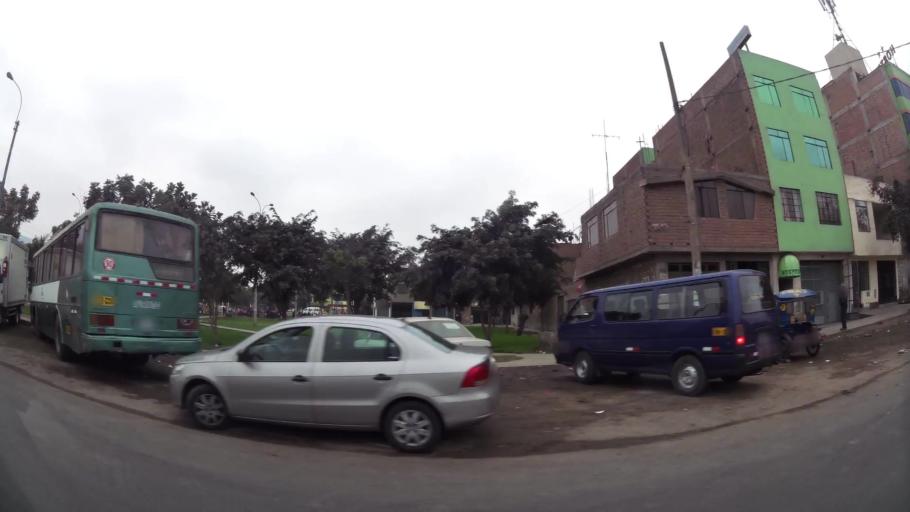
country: PE
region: Lima
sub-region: Lima
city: Vitarte
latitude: -12.0331
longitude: -76.9644
